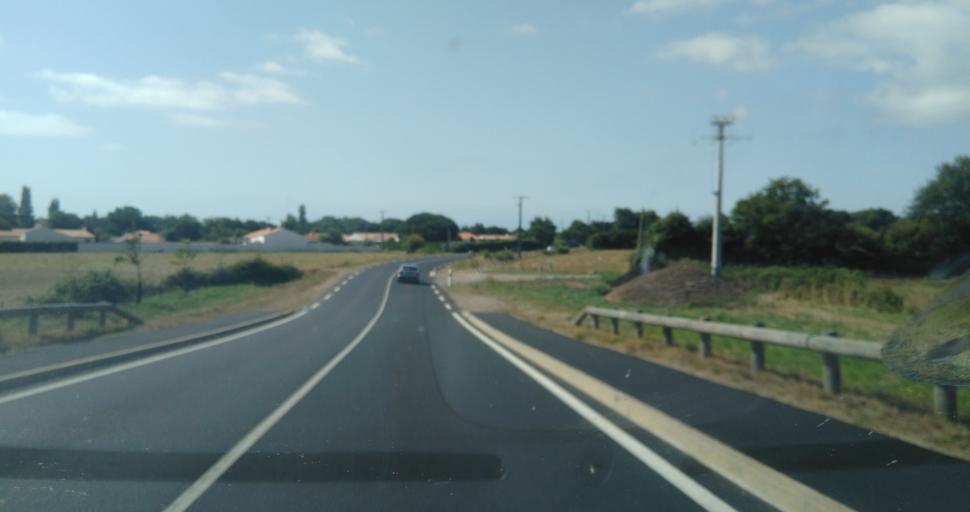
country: FR
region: Pays de la Loire
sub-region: Departement de la Vendee
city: Saint-Hilaire-de-Talmont
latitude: 46.4703
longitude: -1.6491
